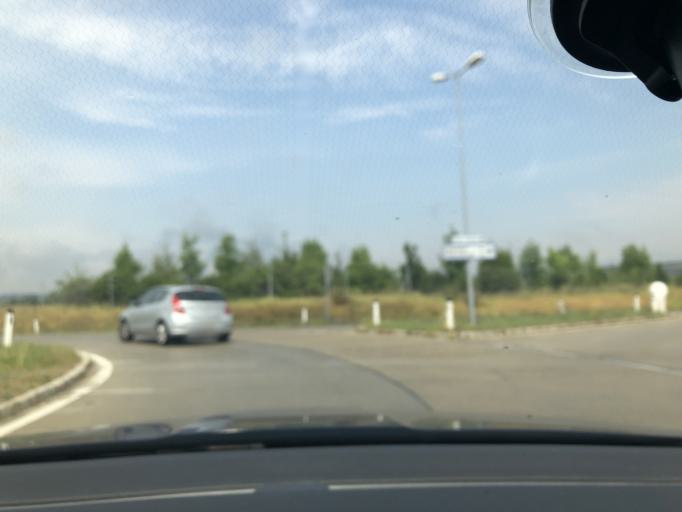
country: AT
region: Lower Austria
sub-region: Politischer Bezirk Mistelbach
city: Gaweinstal
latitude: 48.4863
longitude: 16.5750
